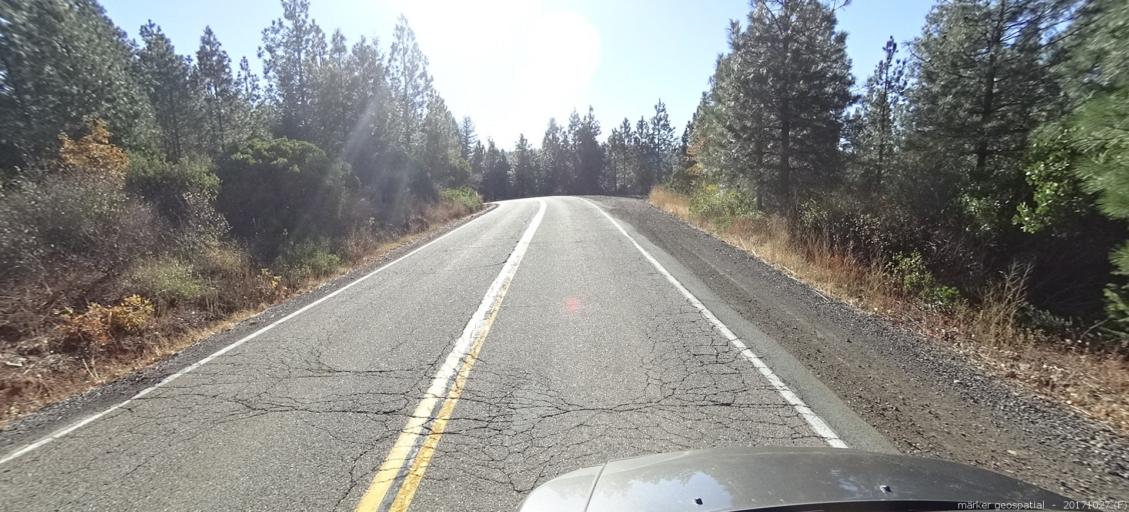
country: US
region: California
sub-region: Shasta County
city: Burney
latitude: 40.8747
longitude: -121.9059
